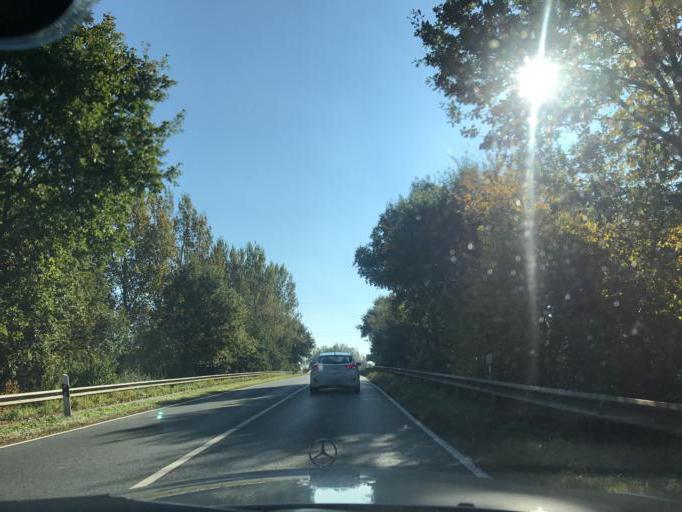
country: DE
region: Lower Saxony
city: Papenburg
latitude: 53.0839
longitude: 7.3756
